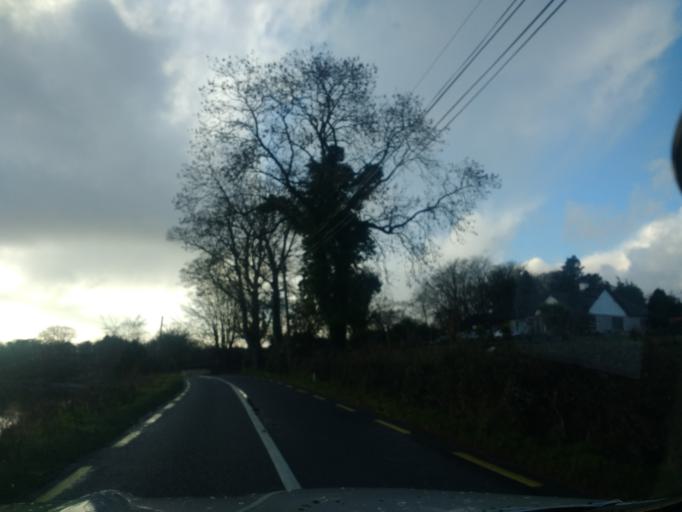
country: IE
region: Ulster
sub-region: County Donegal
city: Ramelton
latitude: 55.0791
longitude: -7.5892
